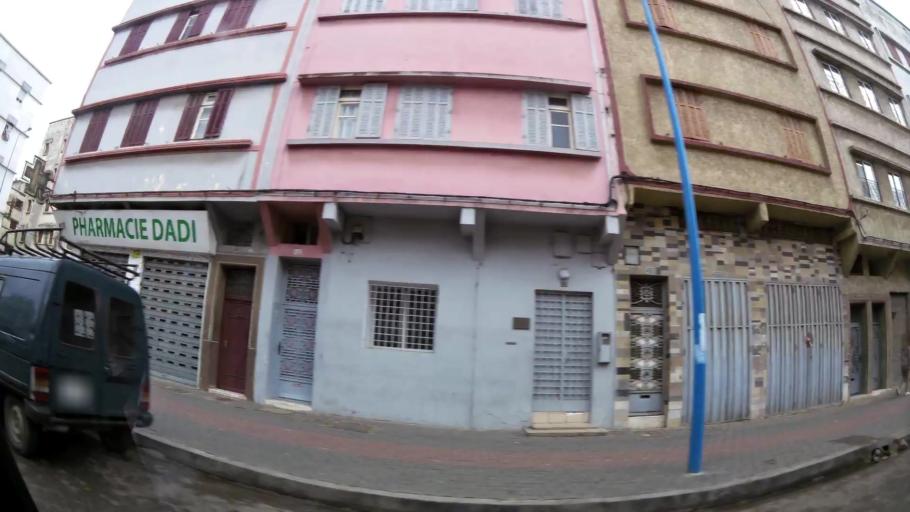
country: MA
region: Grand Casablanca
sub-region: Casablanca
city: Casablanca
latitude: 33.5464
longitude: -7.5723
